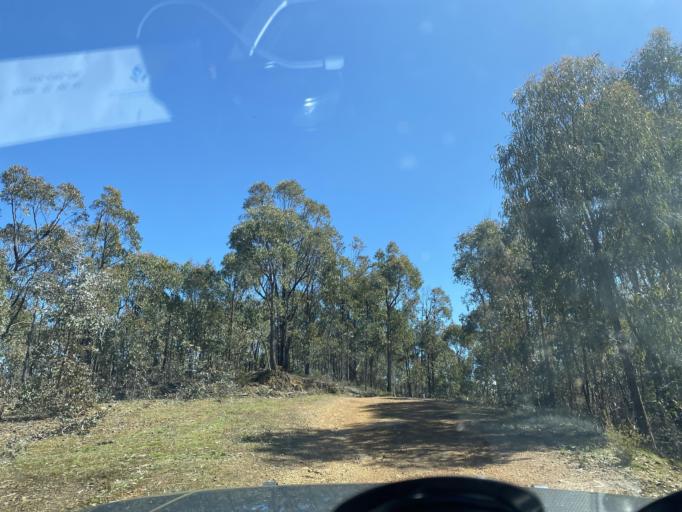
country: AU
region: Victoria
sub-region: Benalla
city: Benalla
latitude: -36.7289
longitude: 146.1816
